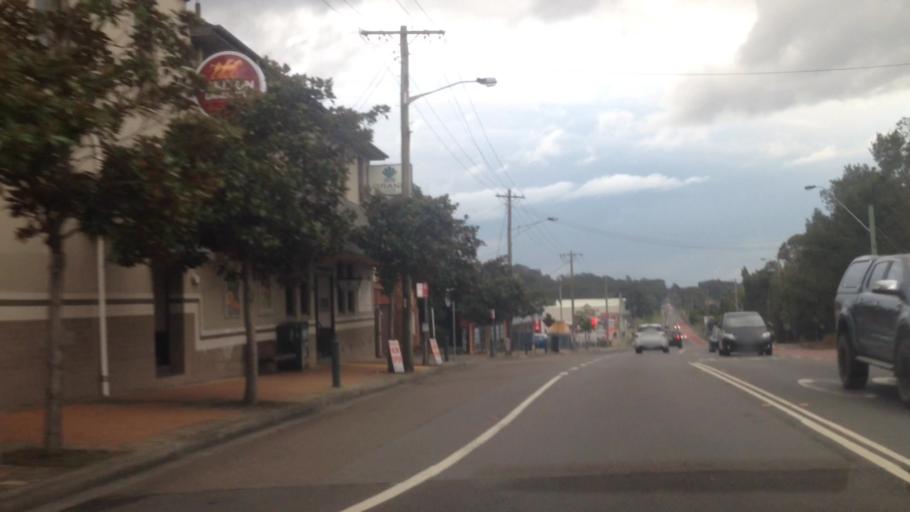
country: AU
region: New South Wales
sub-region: Wyong Shire
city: Chittaway Bay
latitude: -33.2837
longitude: 151.4251
